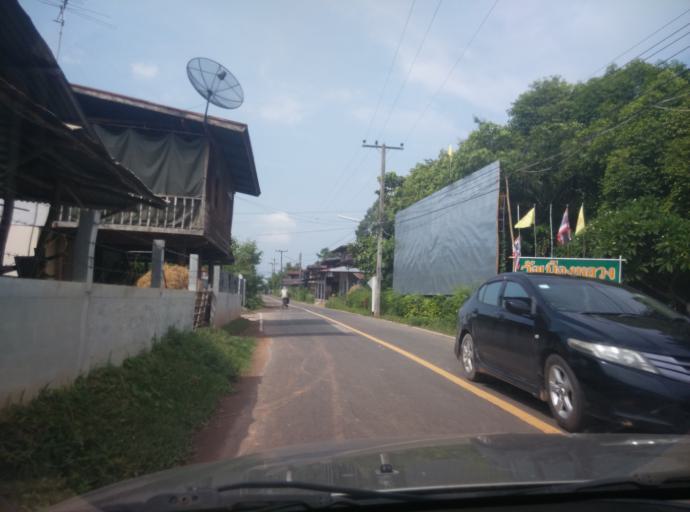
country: TH
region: Sisaket
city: Huai Thap Than
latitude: 15.0291
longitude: 104.0742
